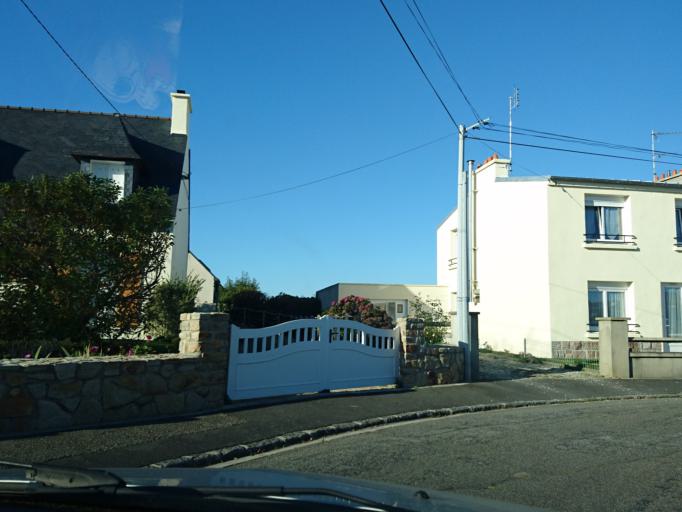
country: FR
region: Brittany
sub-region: Departement du Finistere
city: Brest
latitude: 48.4144
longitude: -4.4526
